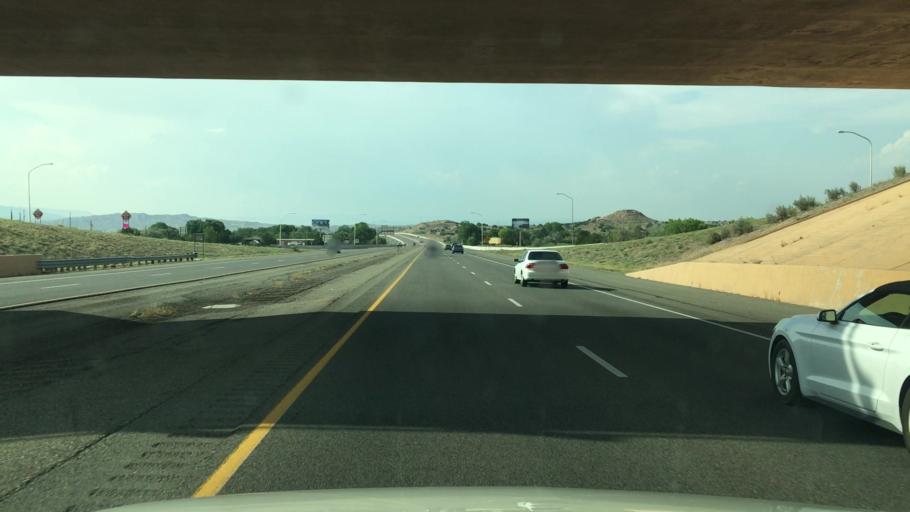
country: US
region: New Mexico
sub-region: Santa Fe County
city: Nambe
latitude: 35.8592
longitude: -105.9992
